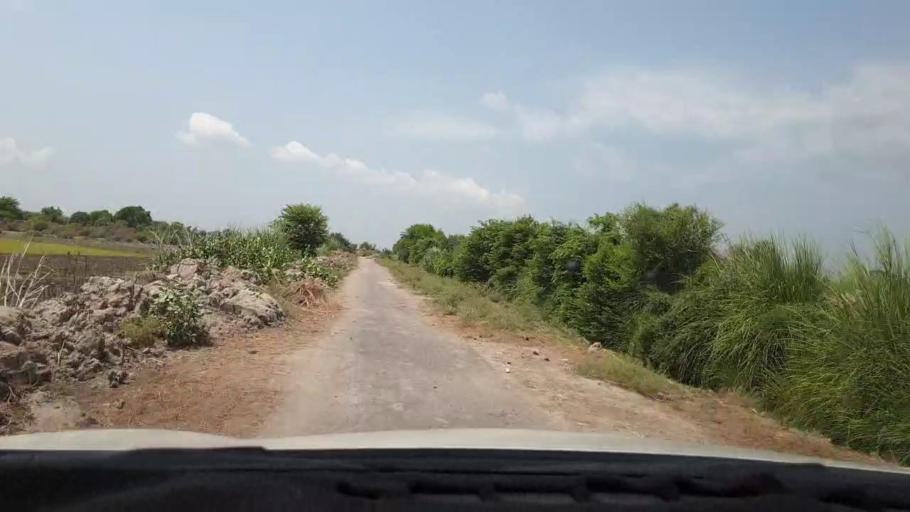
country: PK
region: Sindh
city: Ratodero
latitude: 27.8365
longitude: 68.2173
